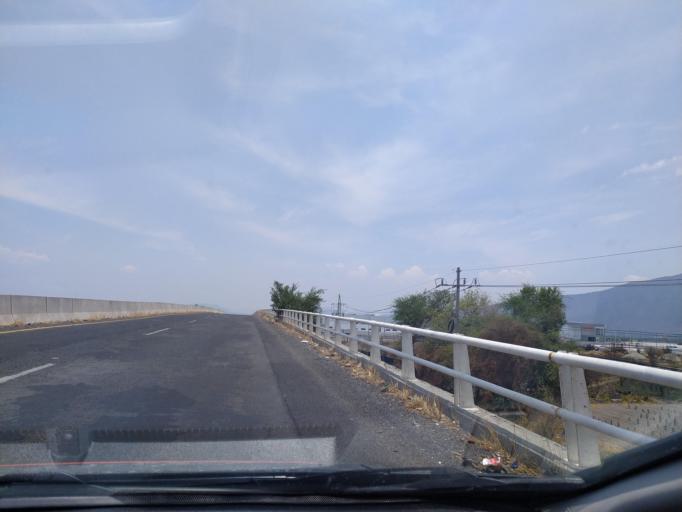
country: MX
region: Jalisco
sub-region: Acatlan de Juarez
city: Villa de los Ninos
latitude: 20.3402
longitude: -103.5910
